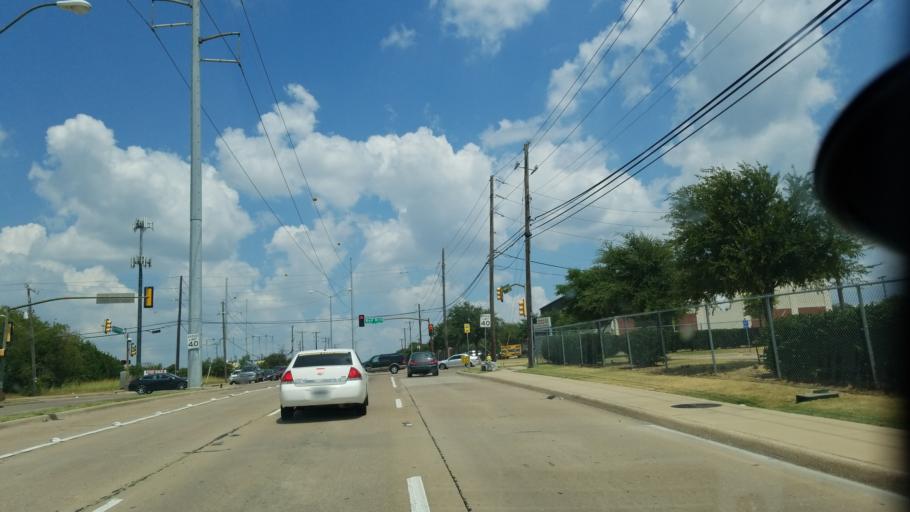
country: US
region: Texas
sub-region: Dallas County
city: Duncanville
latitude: 32.6761
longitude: -96.8827
